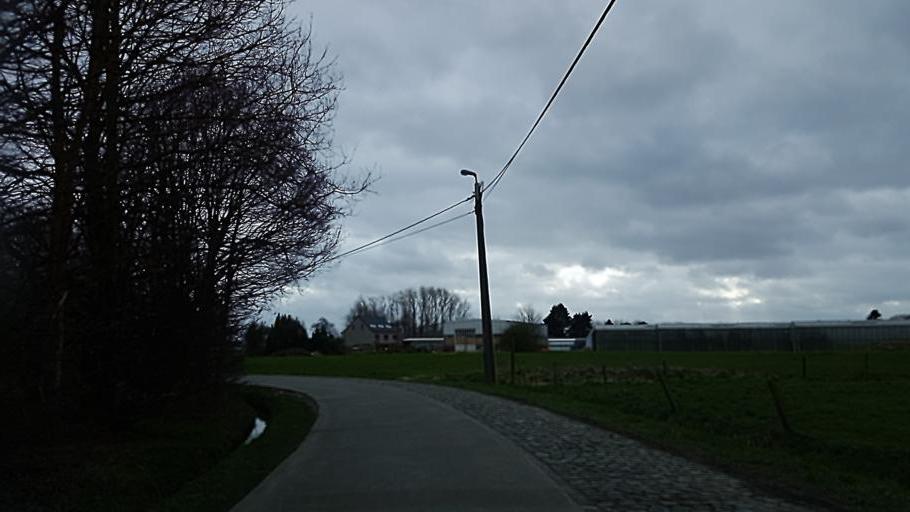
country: BE
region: Flanders
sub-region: Provincie Antwerpen
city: Duffel
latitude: 51.1101
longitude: 4.5022
